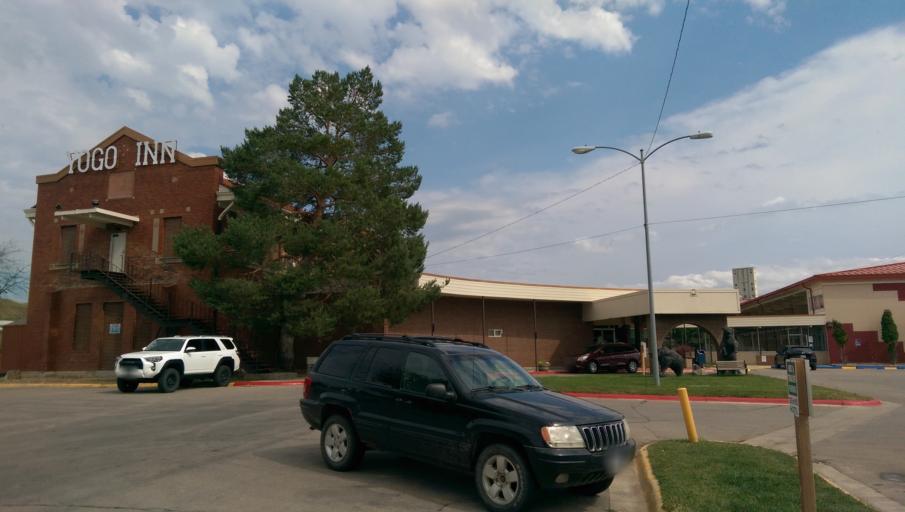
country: US
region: Montana
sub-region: Fergus County
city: Lewistown
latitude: 47.0675
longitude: -109.4222
